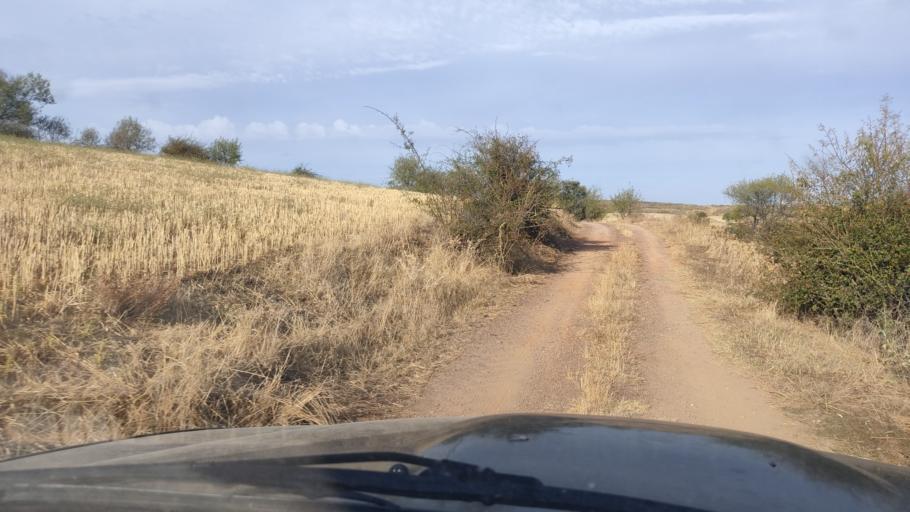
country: ES
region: Aragon
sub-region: Provincia de Teruel
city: Monforte de Moyuela
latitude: 41.0313
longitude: -1.0172
